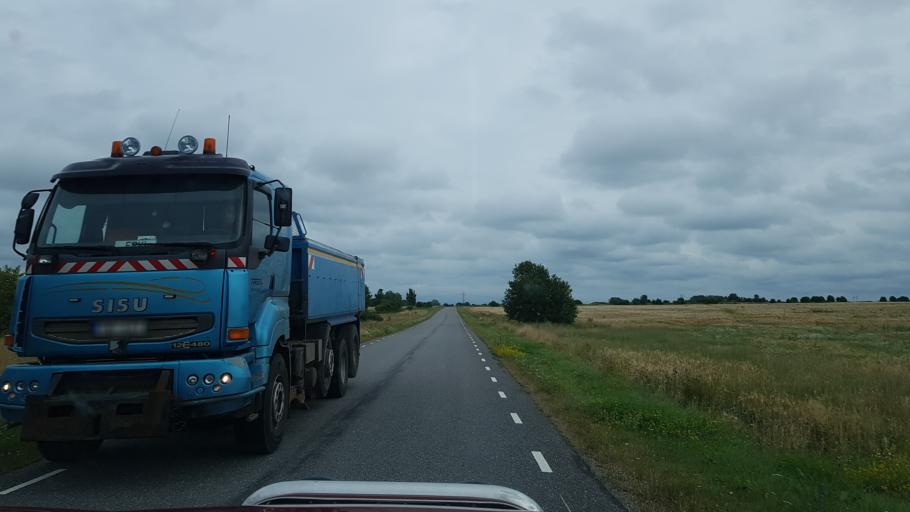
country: EE
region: Ida-Virumaa
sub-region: Puessi linn
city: Pussi
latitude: 59.4036
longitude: 27.0086
